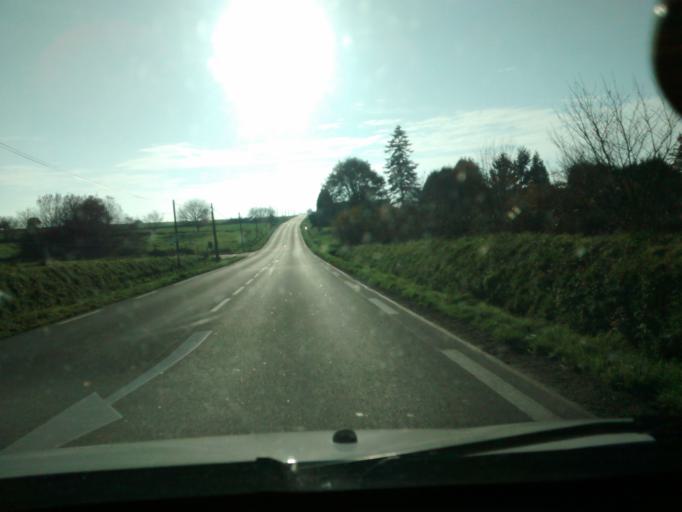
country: FR
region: Brittany
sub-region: Departement d'Ille-et-Vilaine
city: Tremblay
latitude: 48.4113
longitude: -1.4797
